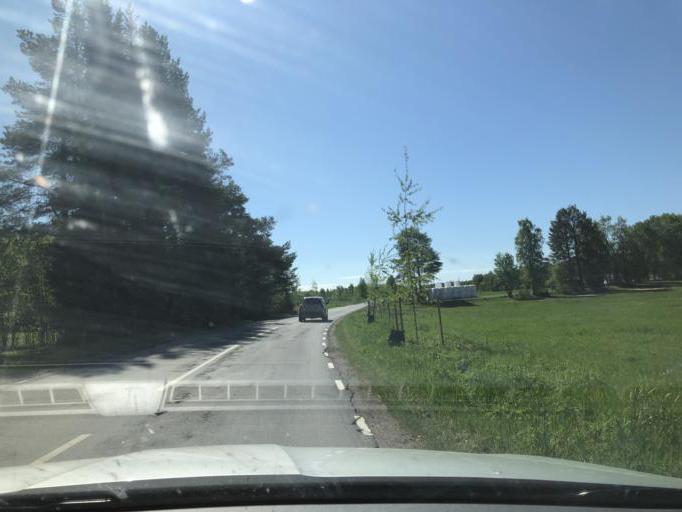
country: SE
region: Norrbotten
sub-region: Lulea Kommun
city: Gammelstad
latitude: 65.6543
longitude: 22.0159
